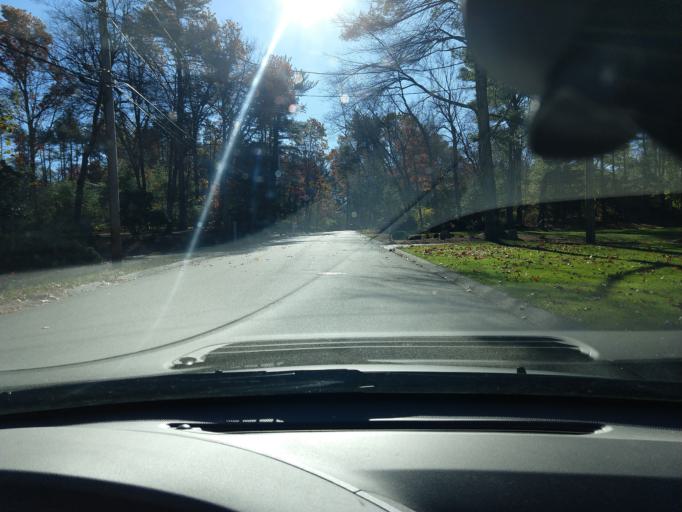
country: US
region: Massachusetts
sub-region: Middlesex County
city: Bedford
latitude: 42.5126
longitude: -71.2624
